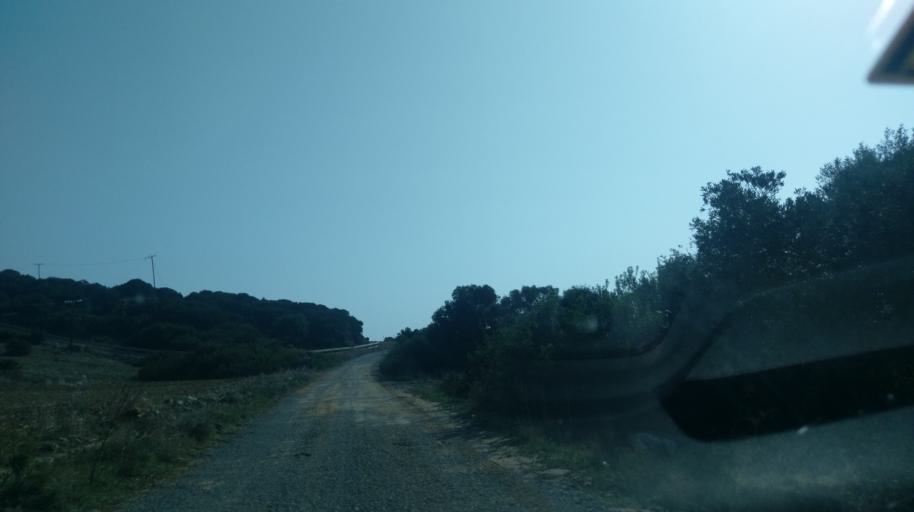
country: CY
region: Ammochostos
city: Rizokarpaso
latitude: 35.6468
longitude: 34.5532
